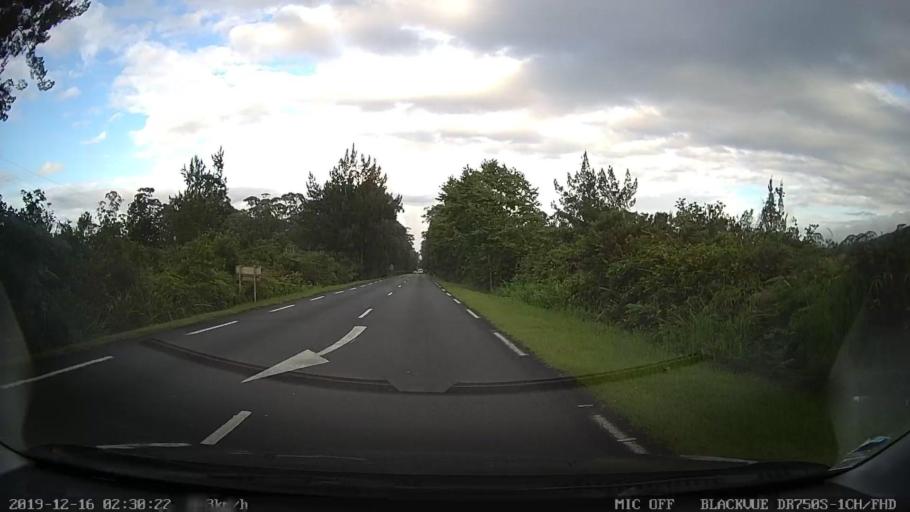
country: RE
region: Reunion
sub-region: Reunion
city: Saint-Benoit
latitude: -21.1104
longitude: 55.6587
